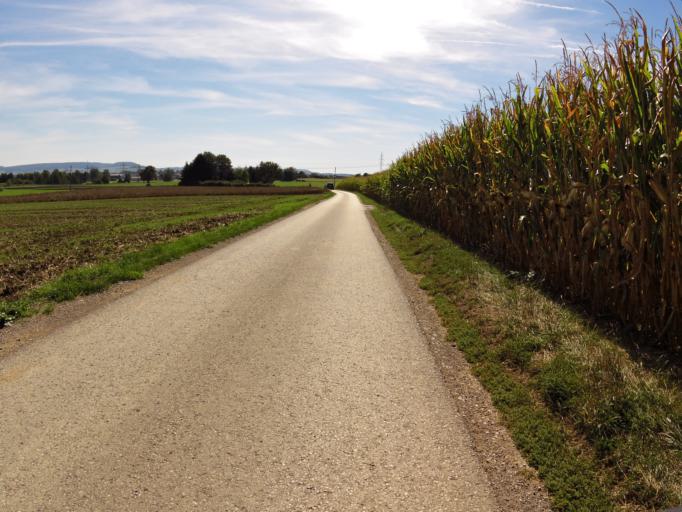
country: DE
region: Baden-Wuerttemberg
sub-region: Freiburg Region
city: Donaueschingen
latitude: 47.9744
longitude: 8.5048
